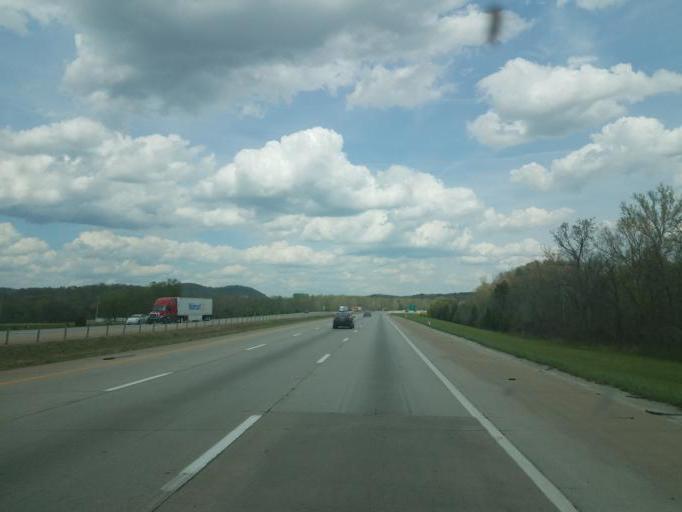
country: US
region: Kentucky
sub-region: Bullitt County
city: Lebanon Junction
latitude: 37.8900
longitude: -85.6992
